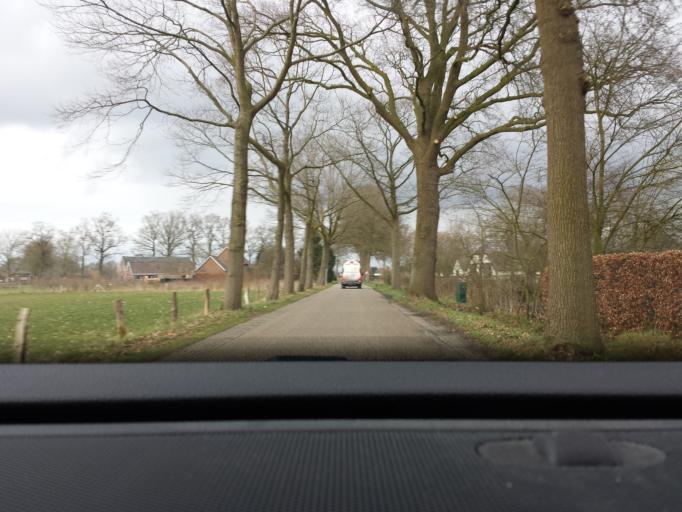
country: NL
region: Gelderland
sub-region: Gemeente Bronckhorst
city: Zelhem
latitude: 51.9727
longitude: 6.3437
